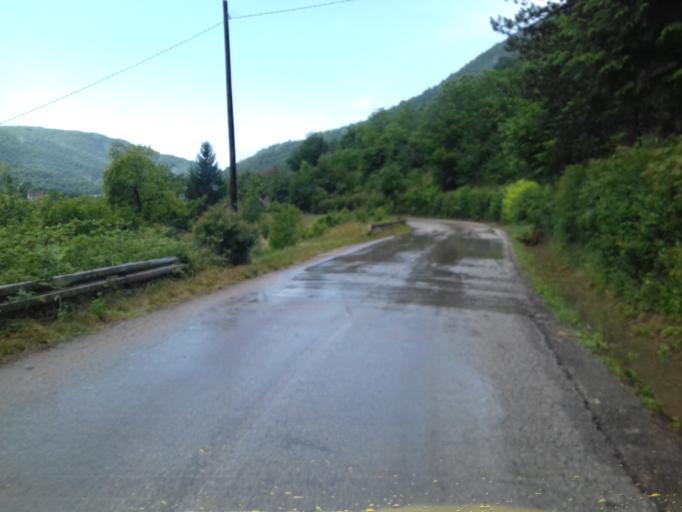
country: BA
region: Federation of Bosnia and Herzegovina
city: Visoko
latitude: 43.9548
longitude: 18.1445
